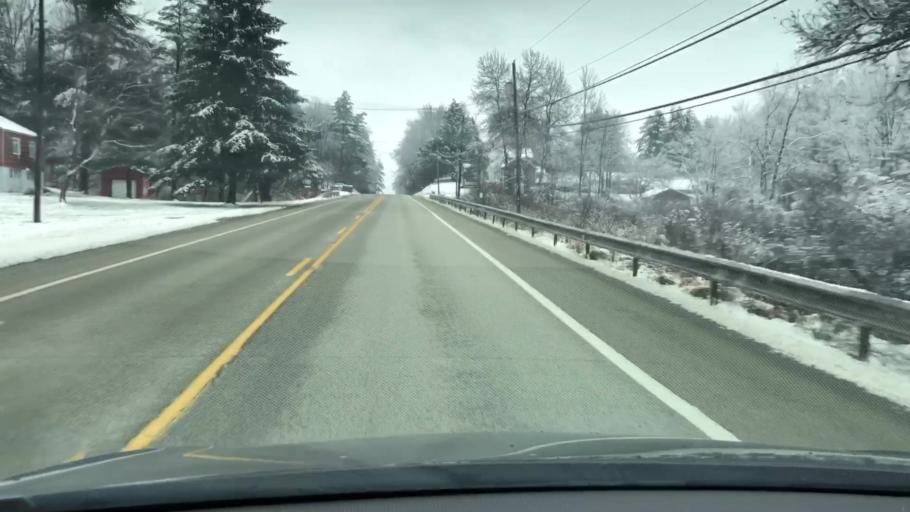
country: US
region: Pennsylvania
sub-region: Fayette County
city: Hopwood
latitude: 39.8120
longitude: -79.5757
